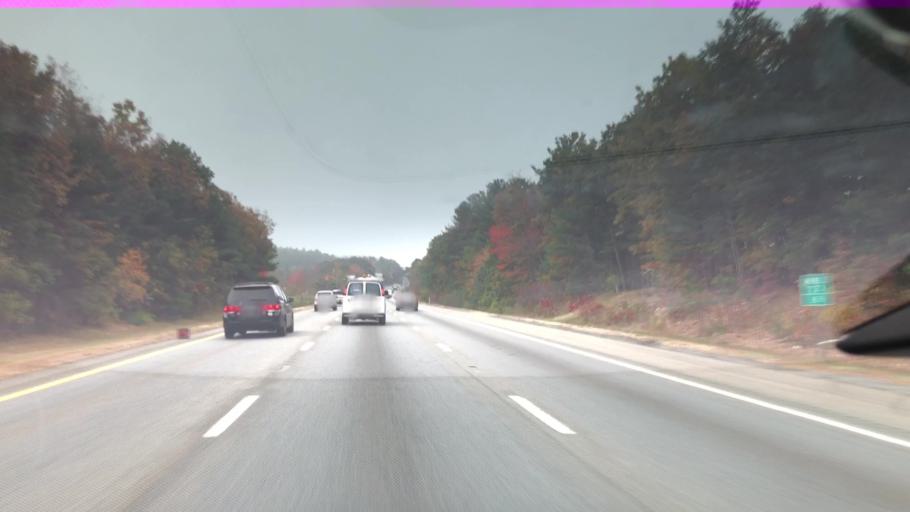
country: US
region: Massachusetts
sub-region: Worcester County
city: Harvard
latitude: 42.4764
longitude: -71.5531
